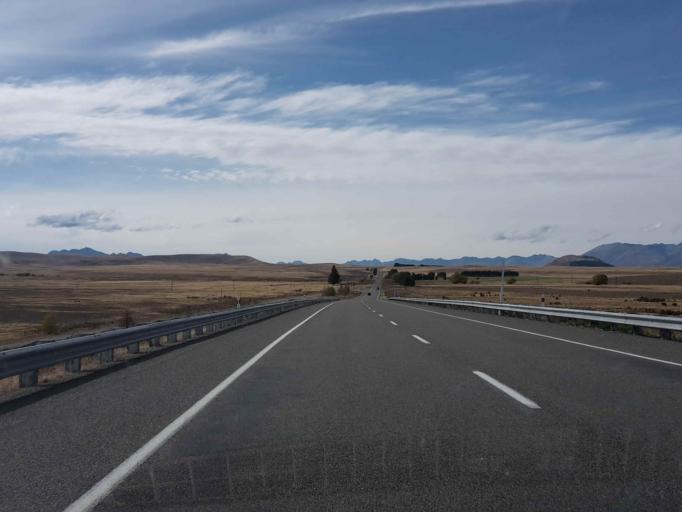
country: NZ
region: Canterbury
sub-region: Timaru District
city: Pleasant Point
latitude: -44.0693
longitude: 170.3599
